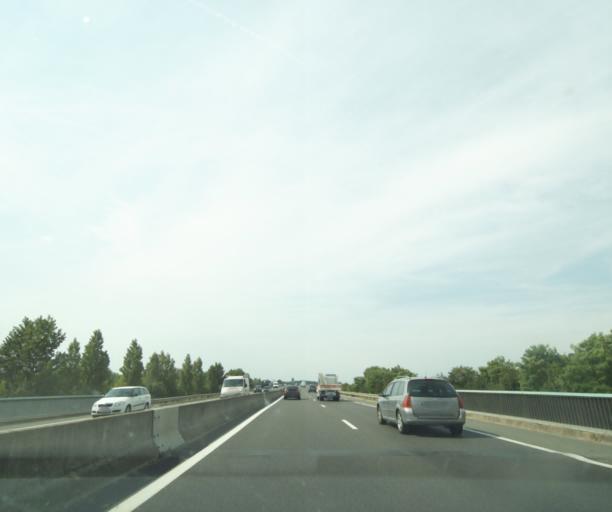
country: FR
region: Centre
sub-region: Departement d'Indre-et-Loire
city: Joue-les-Tours
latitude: 47.3715
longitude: 0.6539
